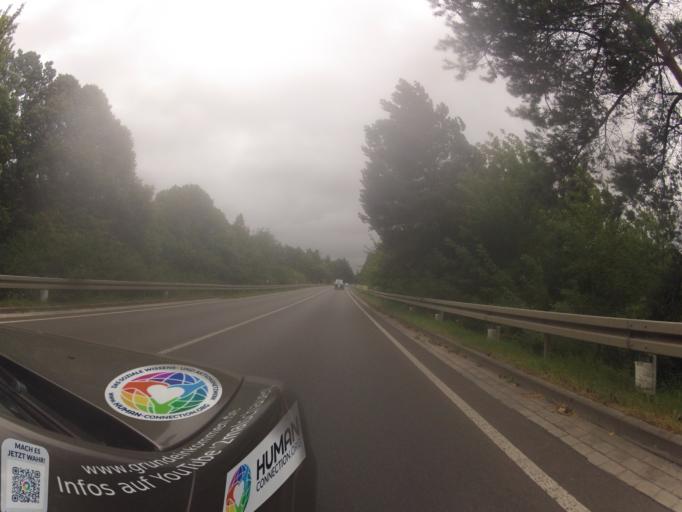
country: DE
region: Mecklenburg-Vorpommern
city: Pasewalk
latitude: 53.4876
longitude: 13.9828
